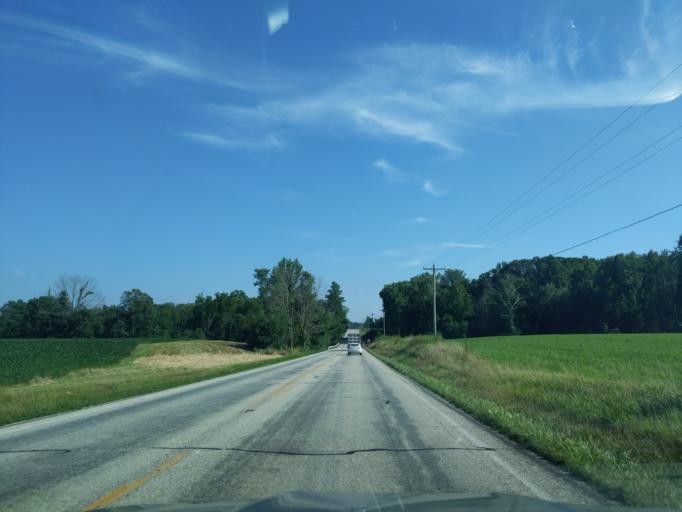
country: US
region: Indiana
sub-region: Ripley County
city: Versailles
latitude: 39.0876
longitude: -85.2750
